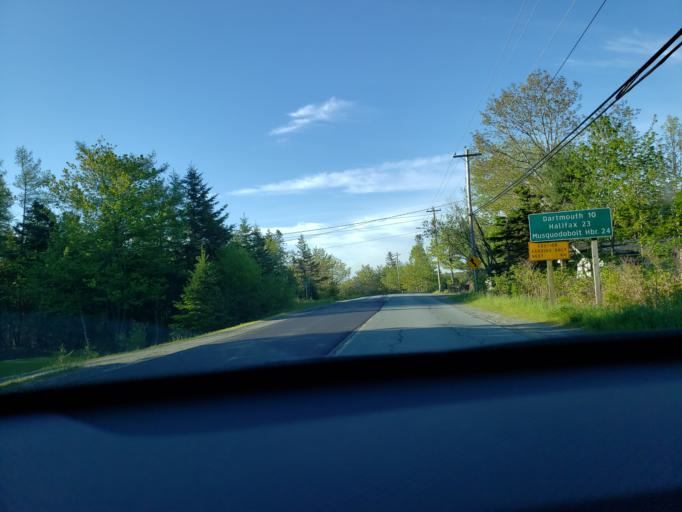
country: CA
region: Nova Scotia
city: Cole Harbour
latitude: 44.7216
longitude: -63.3997
